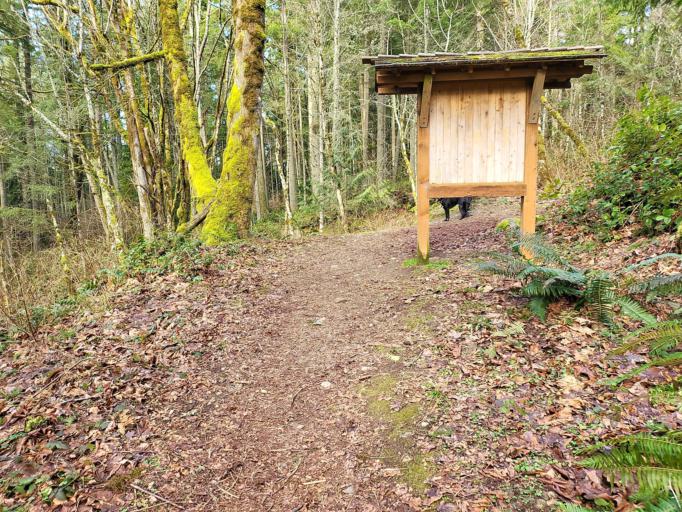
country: US
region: Washington
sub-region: King County
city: Issaquah
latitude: 47.5261
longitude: -122.0219
